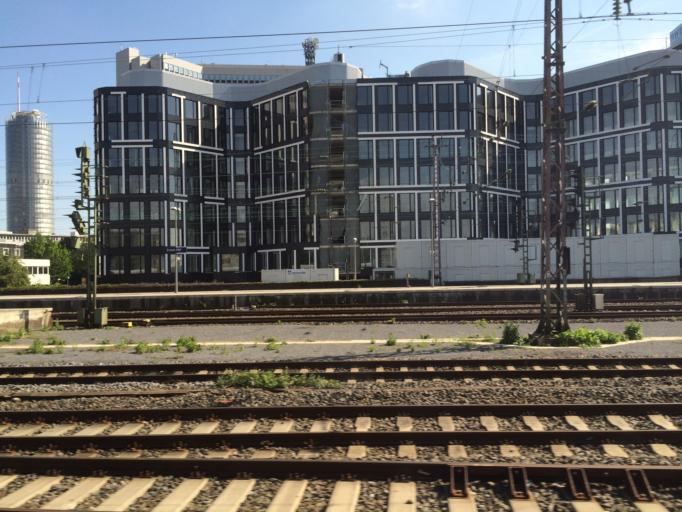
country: DE
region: North Rhine-Westphalia
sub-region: Regierungsbezirk Dusseldorf
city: Essen
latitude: 51.4514
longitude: 7.0099
